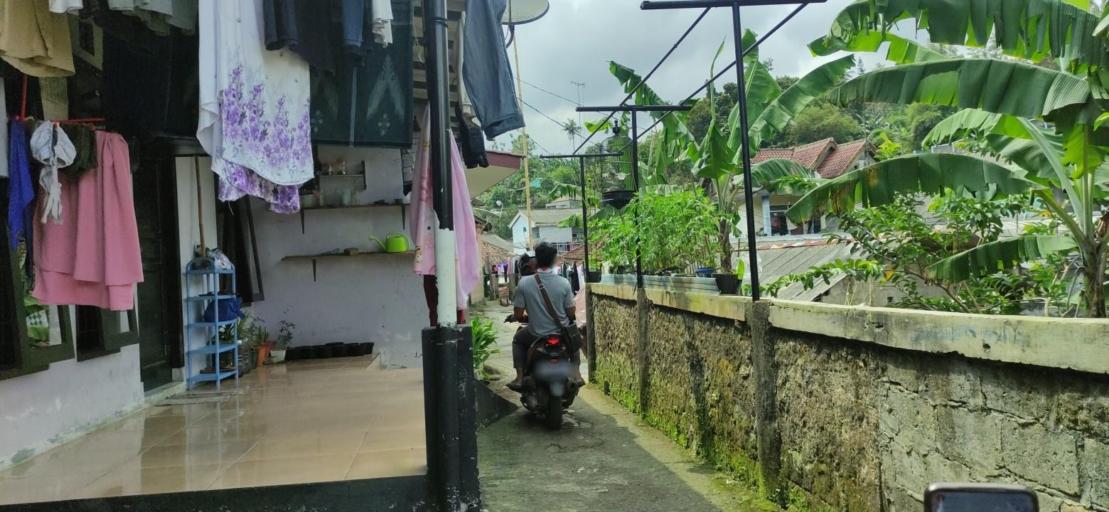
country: ID
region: West Java
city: Caringin
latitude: -6.6474
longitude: 106.8873
